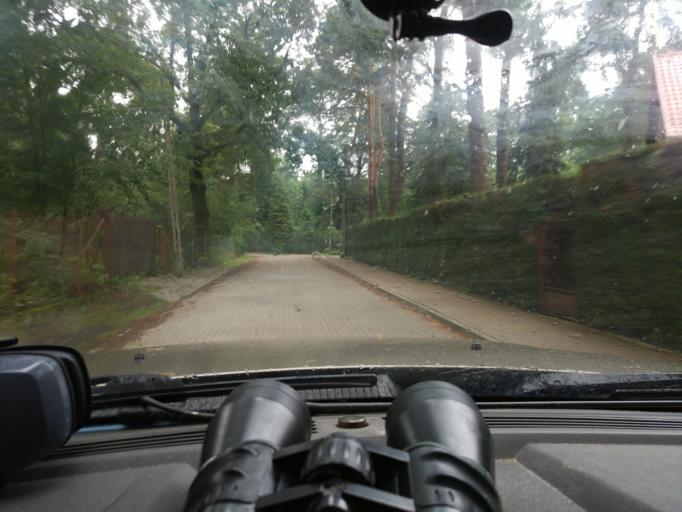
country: PL
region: Masovian Voivodeship
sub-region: Powiat grodziski
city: Podkowa Lesna
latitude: 52.1254
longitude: 20.7372
